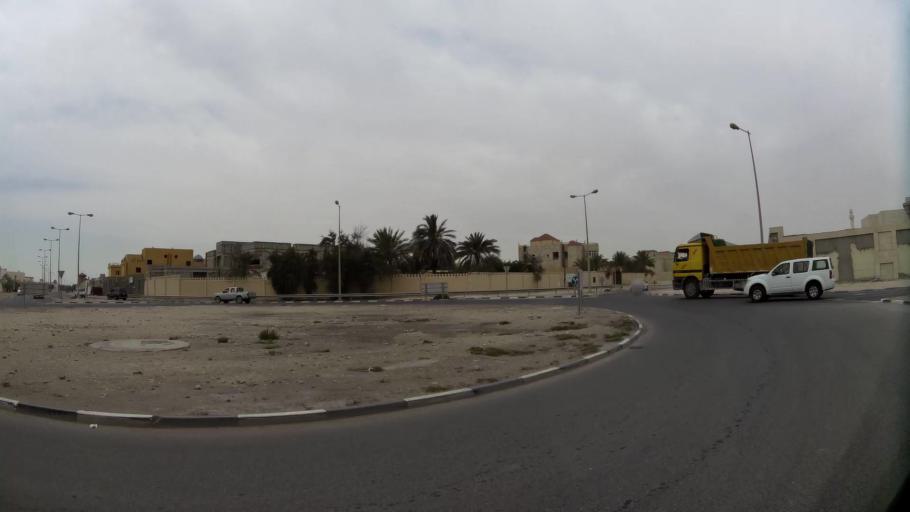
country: QA
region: Baladiyat ar Rayyan
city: Ar Rayyan
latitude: 25.2265
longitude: 51.4592
